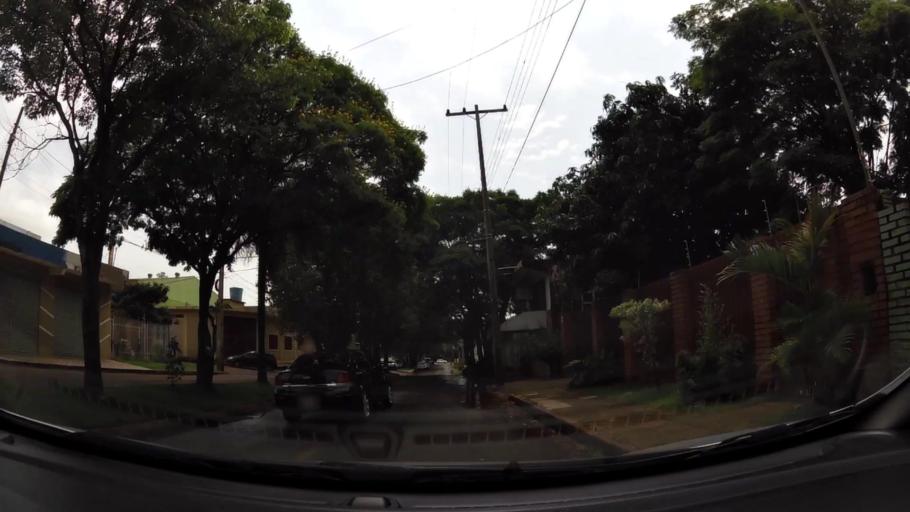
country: PY
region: Alto Parana
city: Ciudad del Este
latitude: -25.5014
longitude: -54.6610
